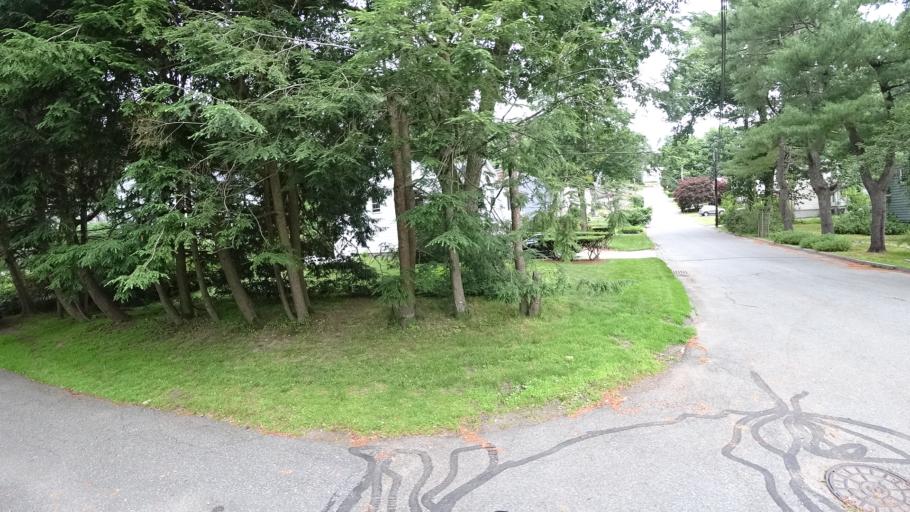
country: US
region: Massachusetts
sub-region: Norfolk County
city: Dedham
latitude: 42.2254
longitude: -71.1512
